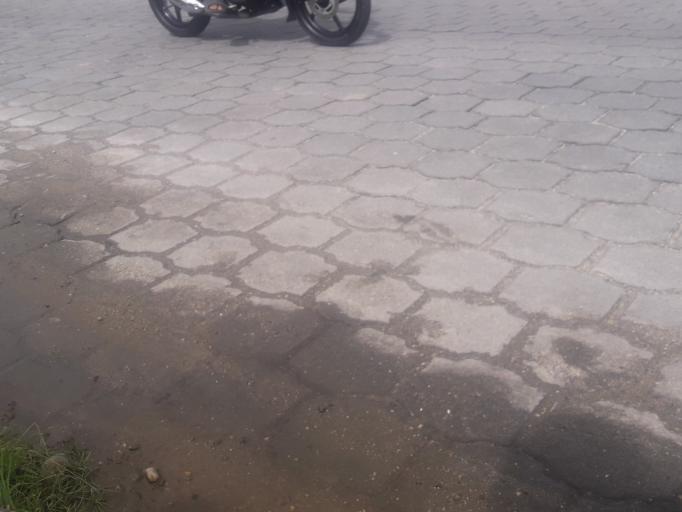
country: EC
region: Napo
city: Tena
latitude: -0.9966
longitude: -77.8115
